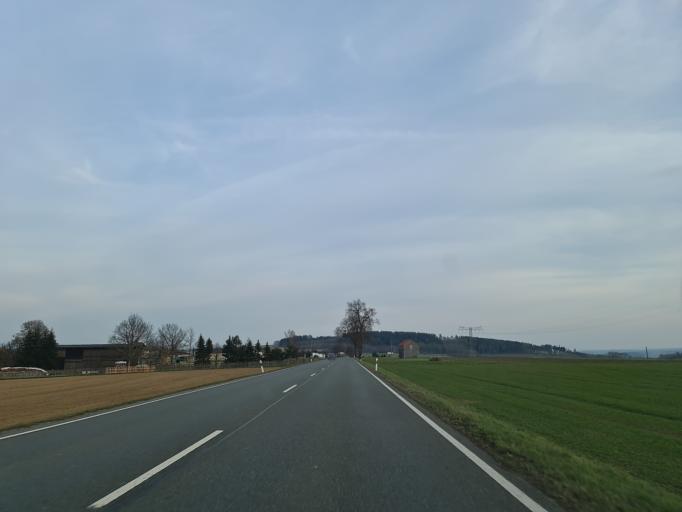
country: DE
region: Saxony
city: Plauen
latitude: 50.4597
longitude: 12.1576
